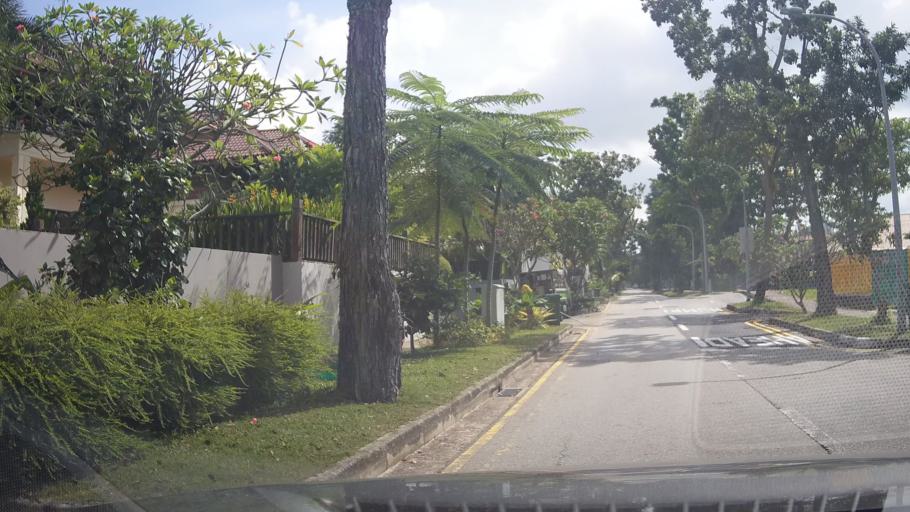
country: SG
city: Singapore
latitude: 1.3023
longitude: 103.8865
